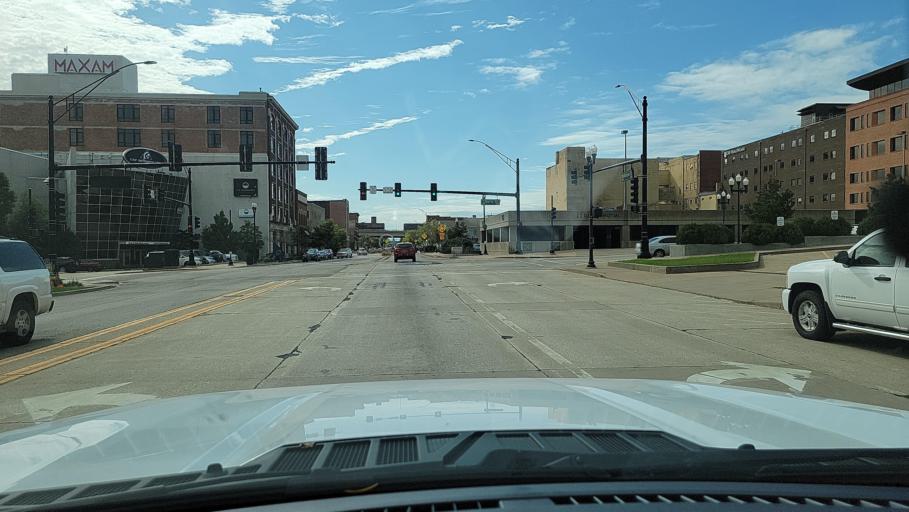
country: US
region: Illinois
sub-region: Peoria County
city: Peoria
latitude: 40.6895
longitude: -89.5907
